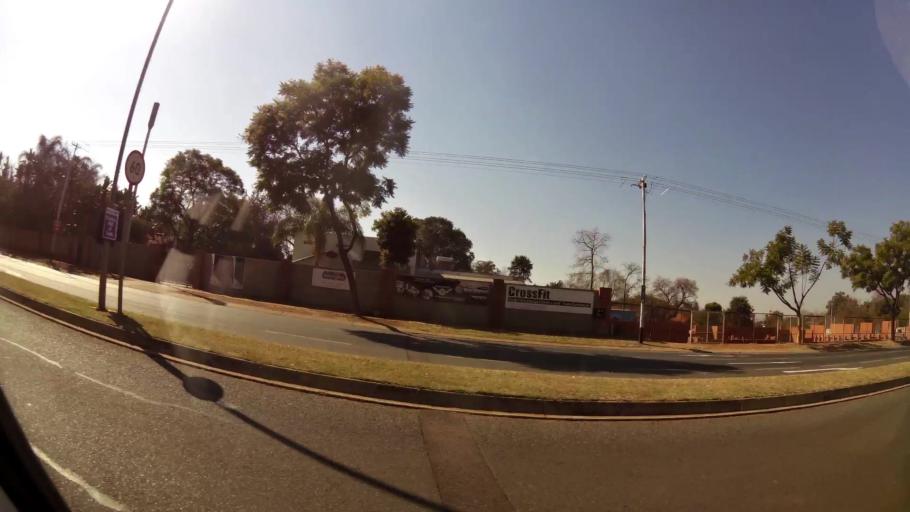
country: ZA
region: Gauteng
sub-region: City of Tshwane Metropolitan Municipality
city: Pretoria
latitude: -25.7696
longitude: 28.2616
